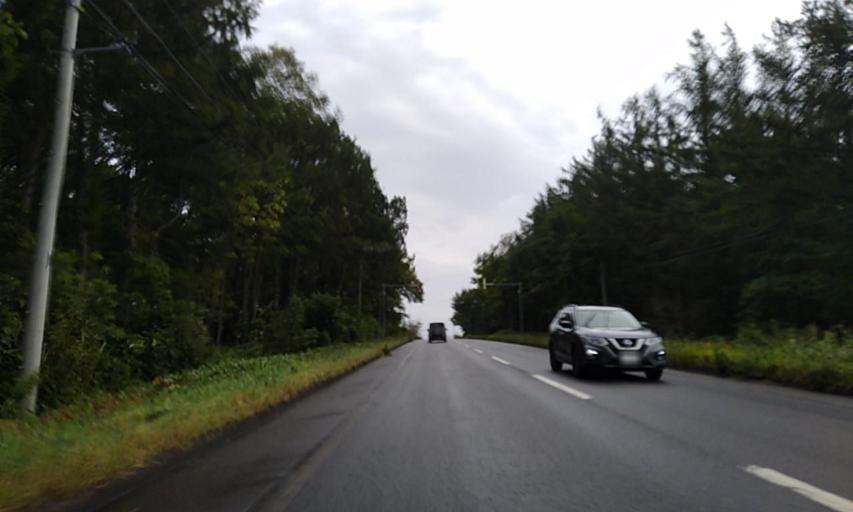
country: JP
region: Hokkaido
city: Abashiri
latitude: 44.1029
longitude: 143.9723
